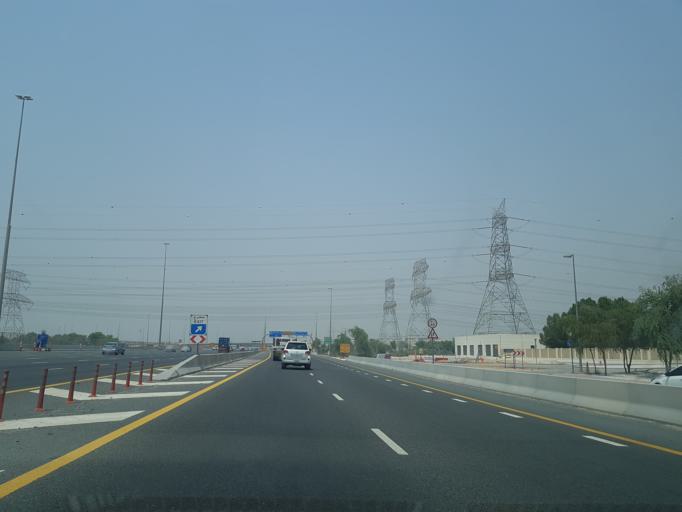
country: AE
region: Ash Shariqah
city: Sharjah
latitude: 25.1550
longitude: 55.3892
